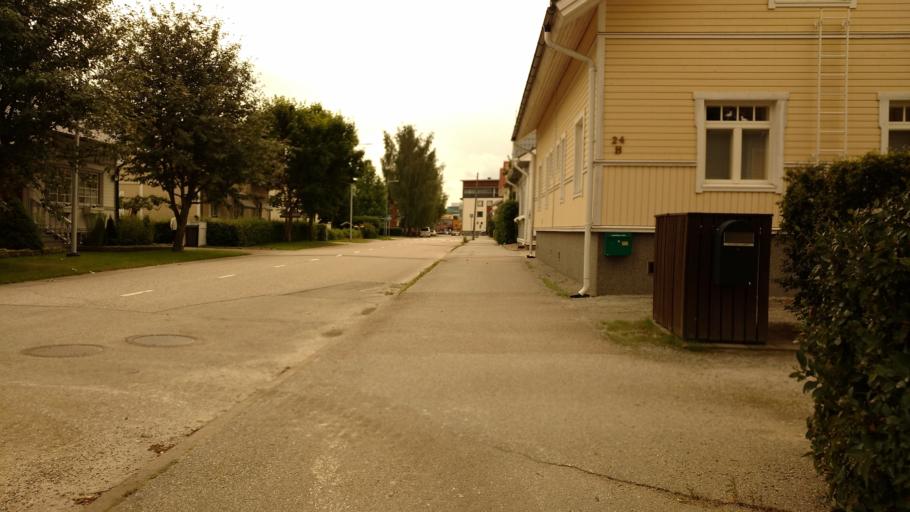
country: FI
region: Varsinais-Suomi
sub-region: Salo
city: Salo
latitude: 60.3911
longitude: 23.1244
